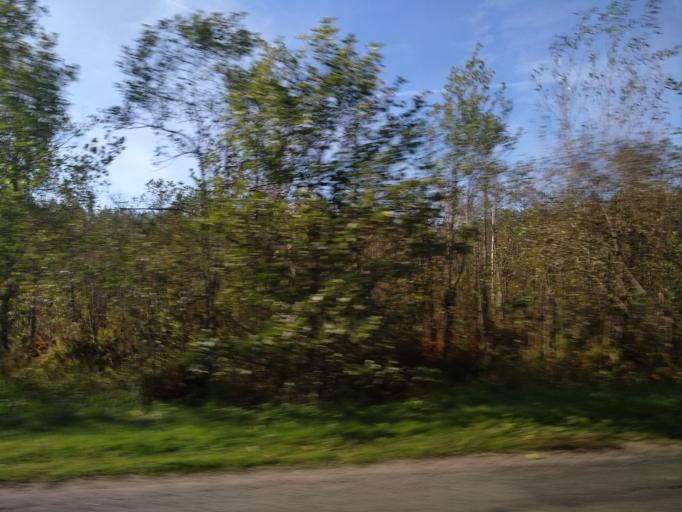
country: BY
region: Vitebsk
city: Mosar
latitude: 55.1416
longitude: 27.1883
